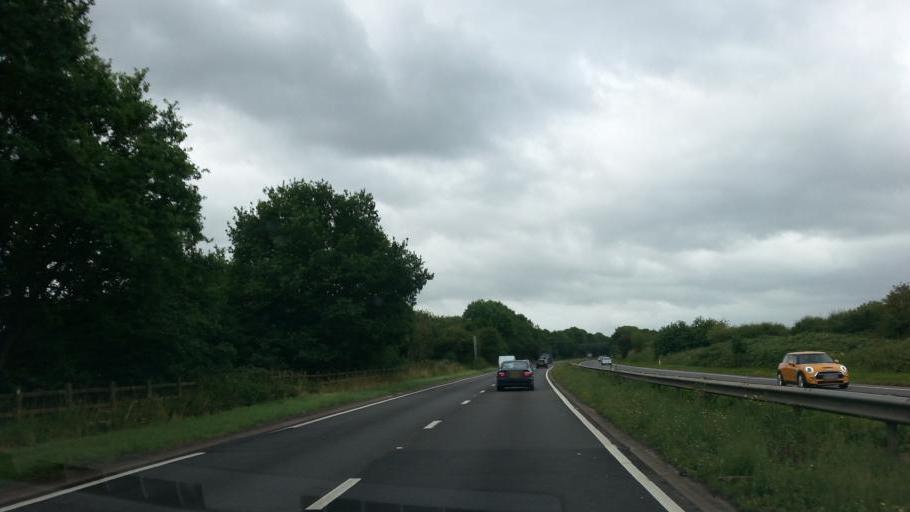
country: GB
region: England
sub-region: Warwickshire
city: Warwick
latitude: 52.3020
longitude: -1.5804
